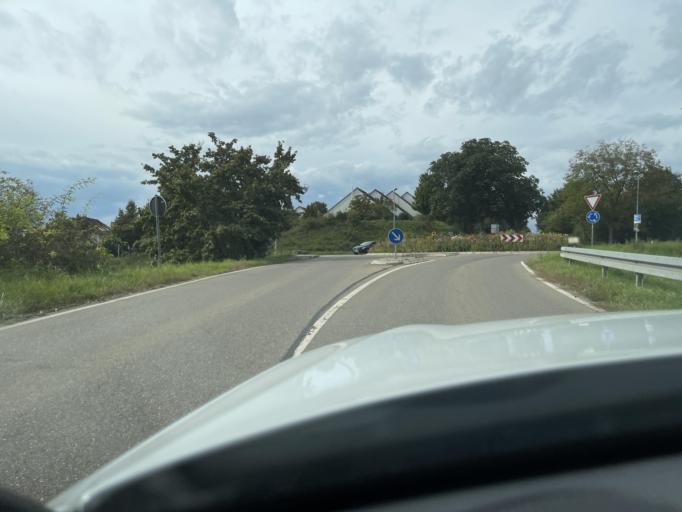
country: DE
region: Baden-Wuerttemberg
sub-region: Regierungsbezirk Stuttgart
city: Marbach am Neckar
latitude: 48.9317
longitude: 9.2653
